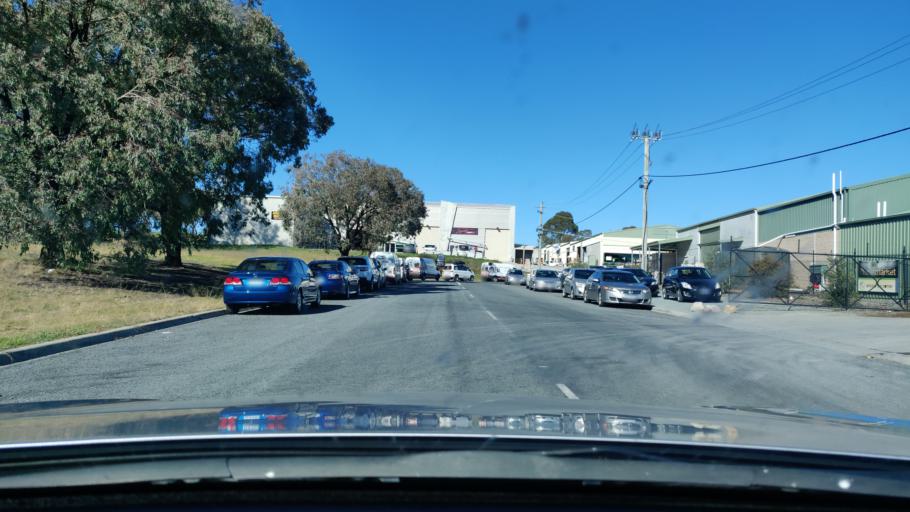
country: AU
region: Australian Capital Territory
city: Macarthur
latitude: -35.3916
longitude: 149.1691
